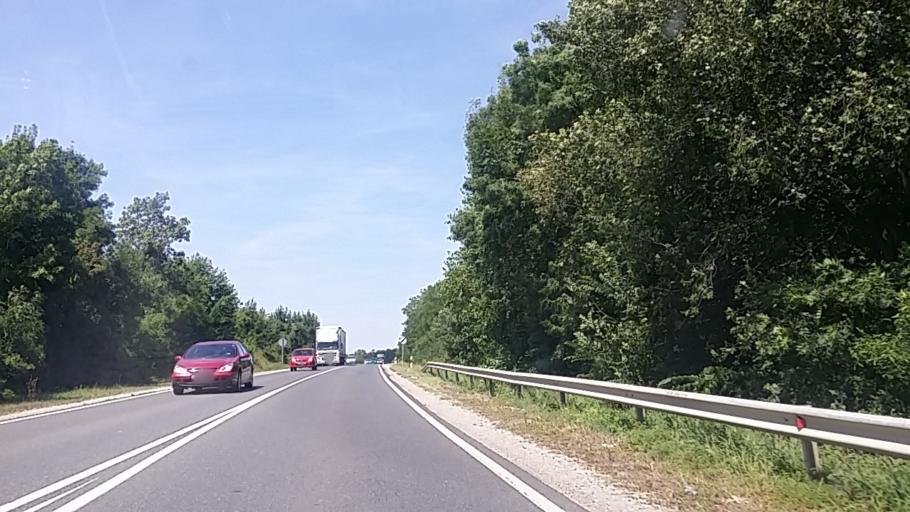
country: HU
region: Fejer
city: Deg
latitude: 46.8625
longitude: 18.4215
